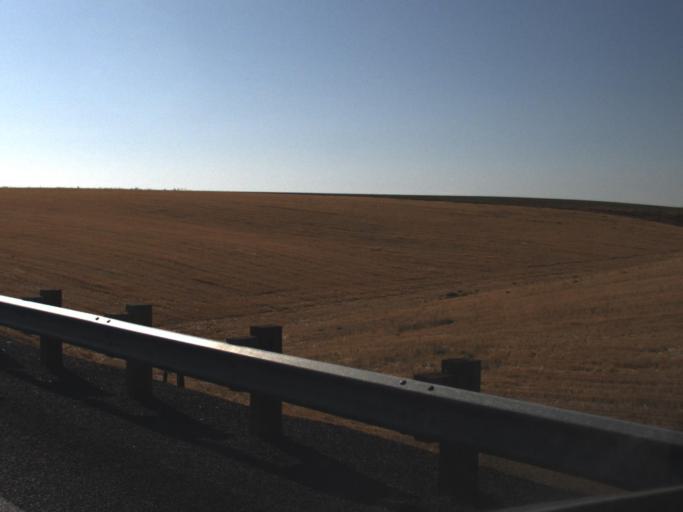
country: US
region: Washington
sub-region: Franklin County
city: Connell
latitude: 46.6225
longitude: -118.7166
